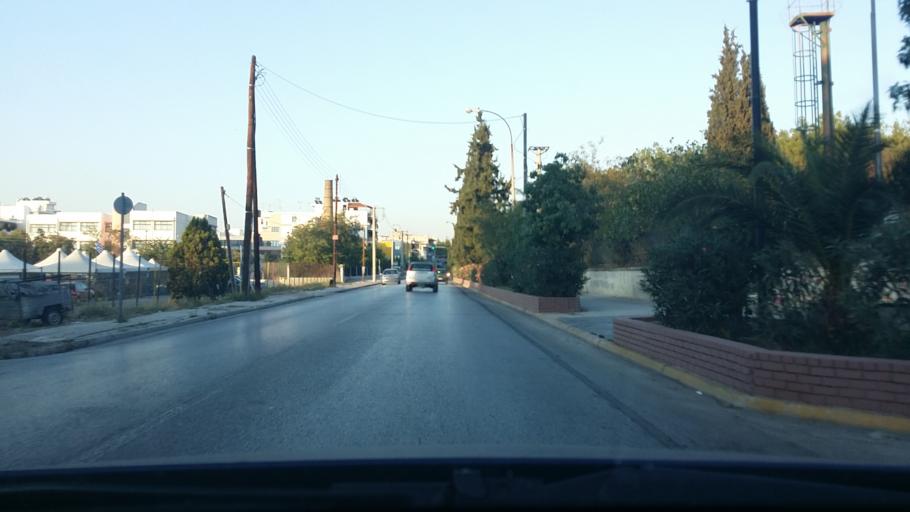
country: GR
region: Attica
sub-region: Nomarchia Athinas
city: Nea Filadelfeia
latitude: 38.0464
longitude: 23.7453
